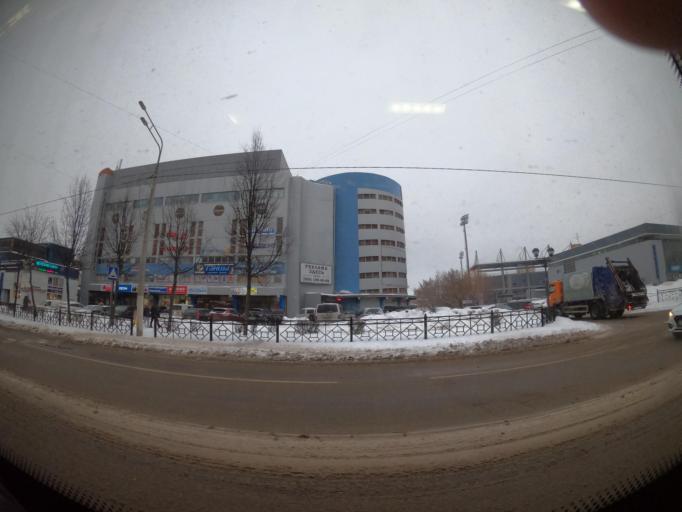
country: RU
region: Moskovskaya
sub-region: Podol'skiy Rayon
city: Podol'sk
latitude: 55.4228
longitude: 37.5288
